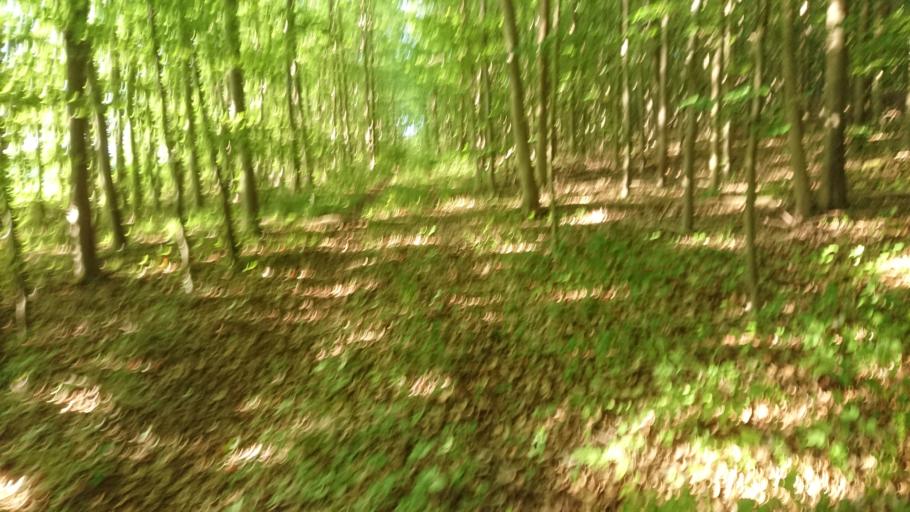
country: DE
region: Lower Saxony
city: Hardegsen
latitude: 51.6022
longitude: 9.8383
